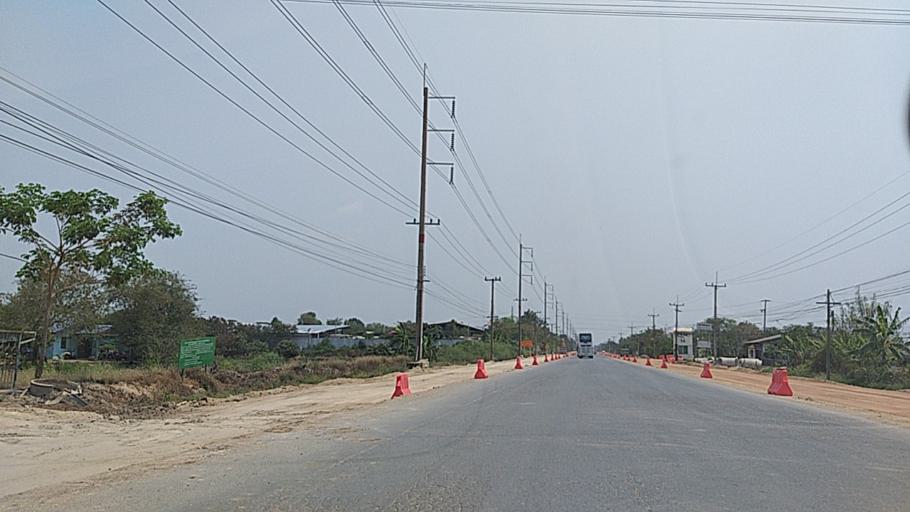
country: TH
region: Chachoengsao
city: Ban Pho
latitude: 13.5738
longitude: 101.1266
